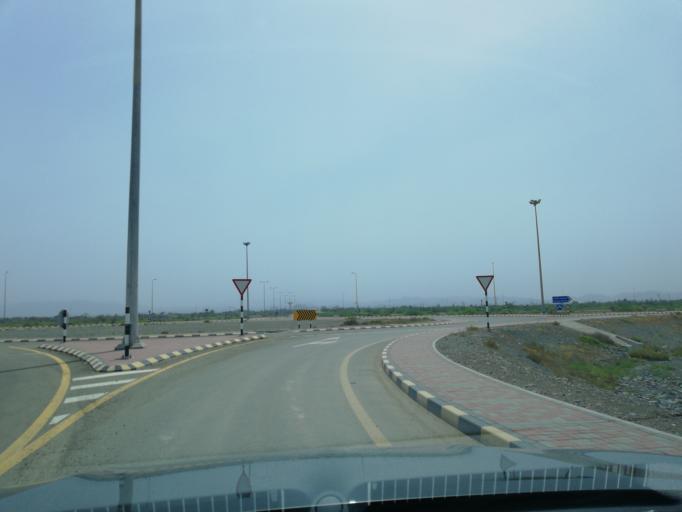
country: OM
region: Al Batinah
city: Shinas
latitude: 24.8641
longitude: 56.4136
